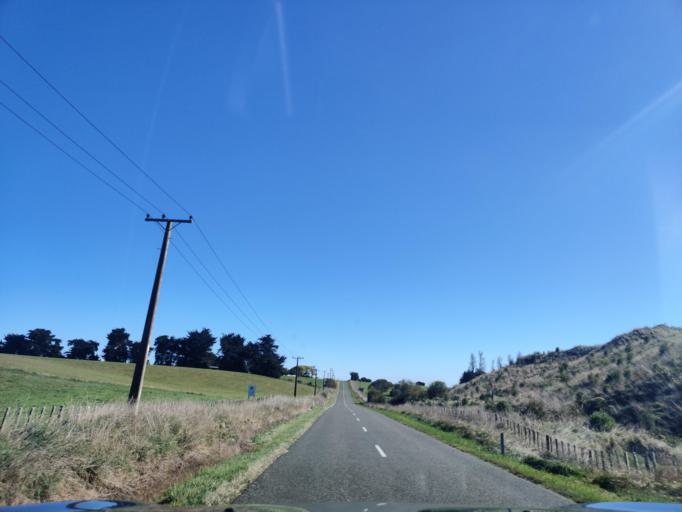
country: NZ
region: Manawatu-Wanganui
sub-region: Palmerston North City
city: Palmerston North
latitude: -40.2467
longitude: 175.6796
